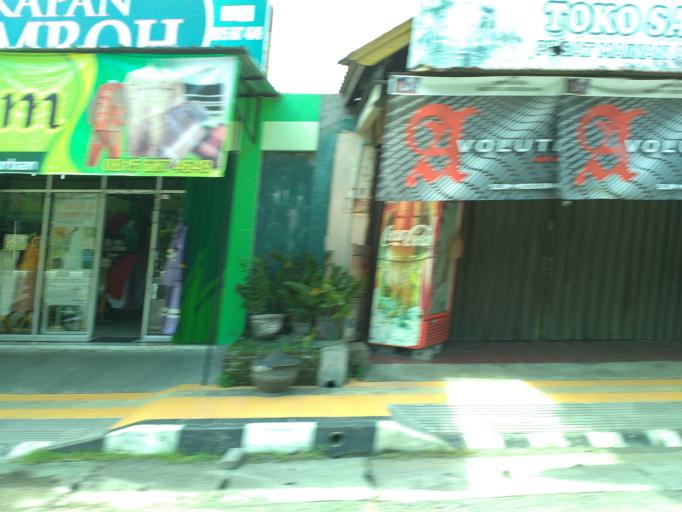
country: ID
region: Central Java
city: Candi Prambanan
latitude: -7.7553
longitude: 110.4927
